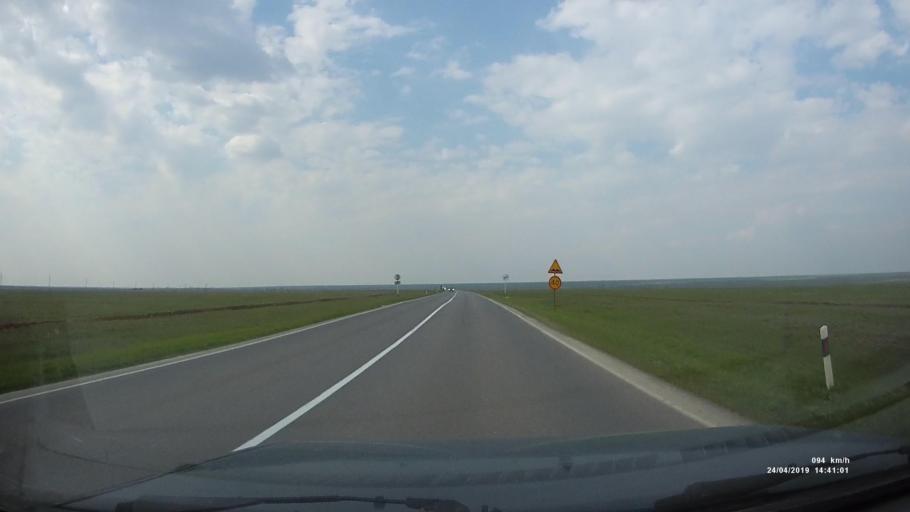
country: RU
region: Rostov
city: Remontnoye
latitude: 46.4401
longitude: 43.8840
